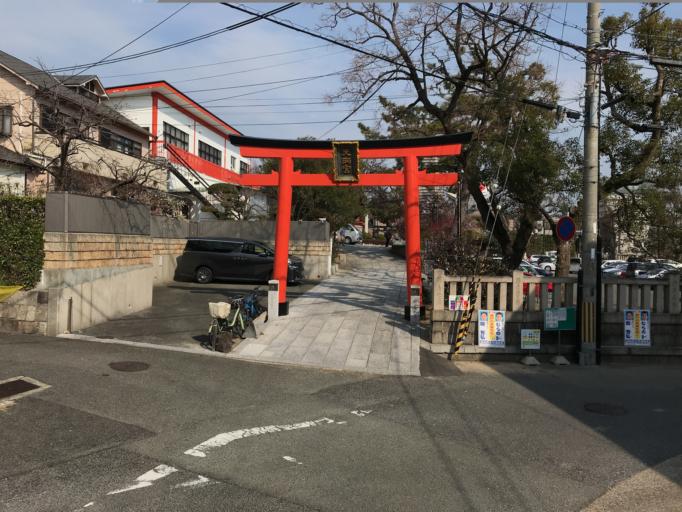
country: JP
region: Hyogo
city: Kobe
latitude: 34.6443
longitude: 135.1186
